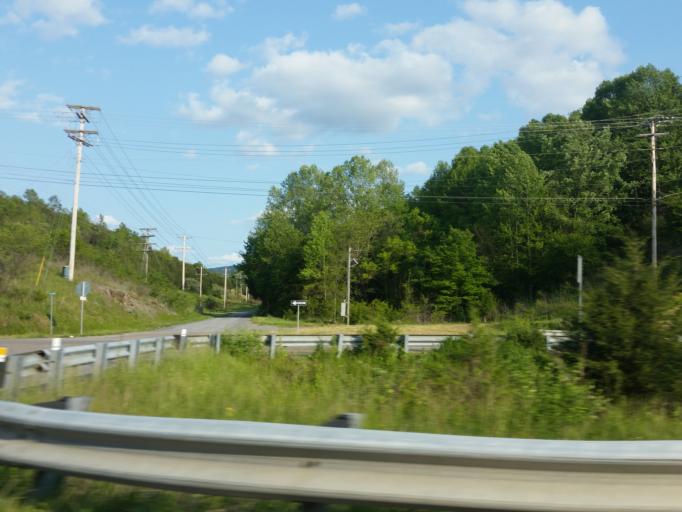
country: US
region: Virginia
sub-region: Tazewell County
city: Claypool Hill
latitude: 37.0488
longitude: -81.7784
